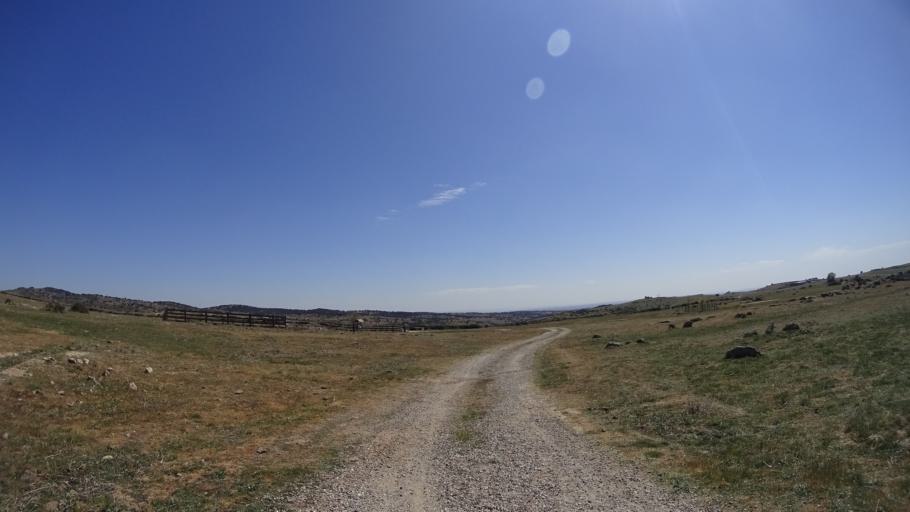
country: ES
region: Madrid
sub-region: Provincia de Madrid
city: Colmenar Viejo
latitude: 40.7011
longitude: -3.7516
